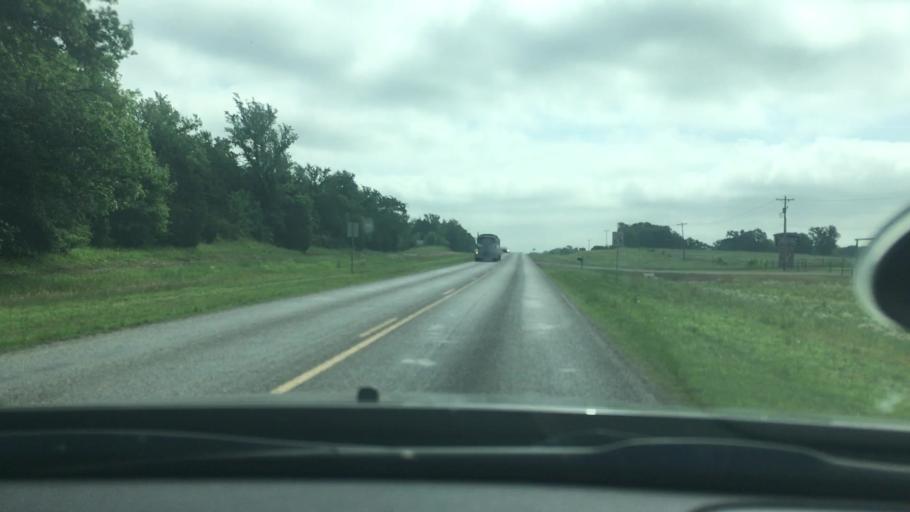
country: US
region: Oklahoma
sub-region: Johnston County
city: Tishomingo
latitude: 34.2304
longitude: -96.6537
